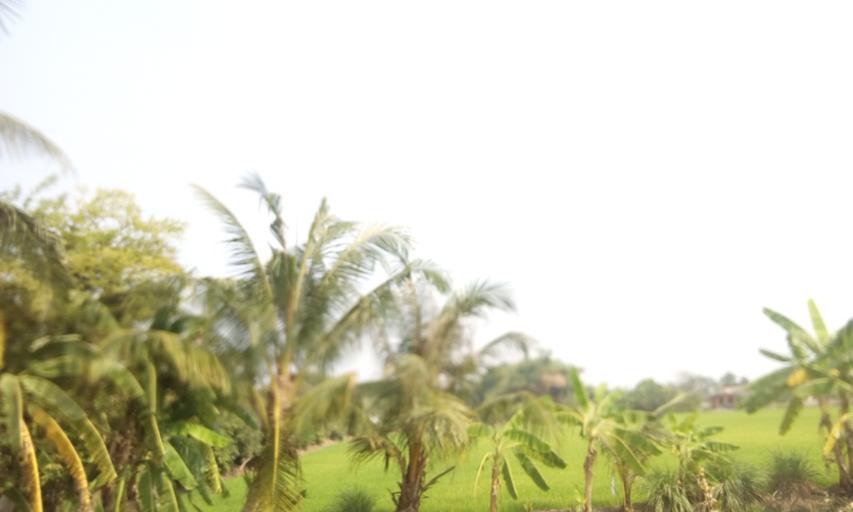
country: TH
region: Pathum Thani
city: Lam Luk Ka
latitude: 13.9526
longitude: 100.7250
